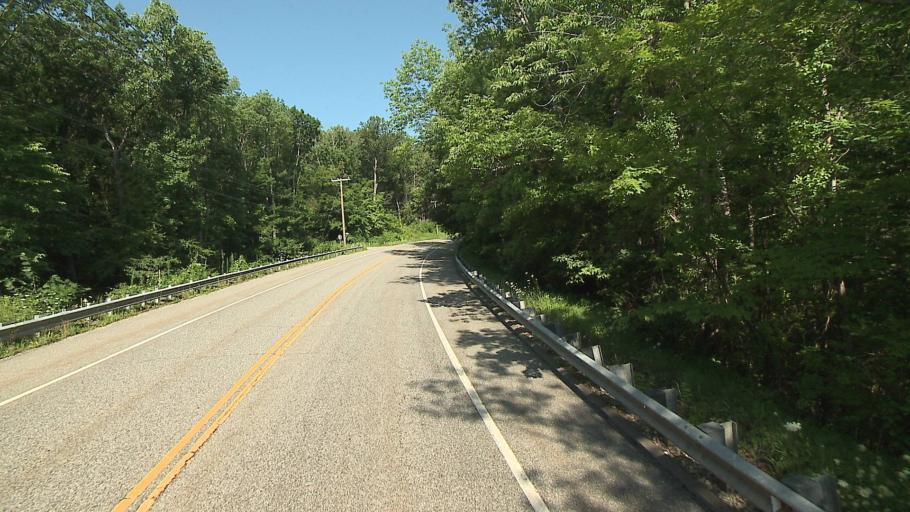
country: US
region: Connecticut
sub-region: Litchfield County
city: Kent
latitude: 41.8212
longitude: -73.3828
